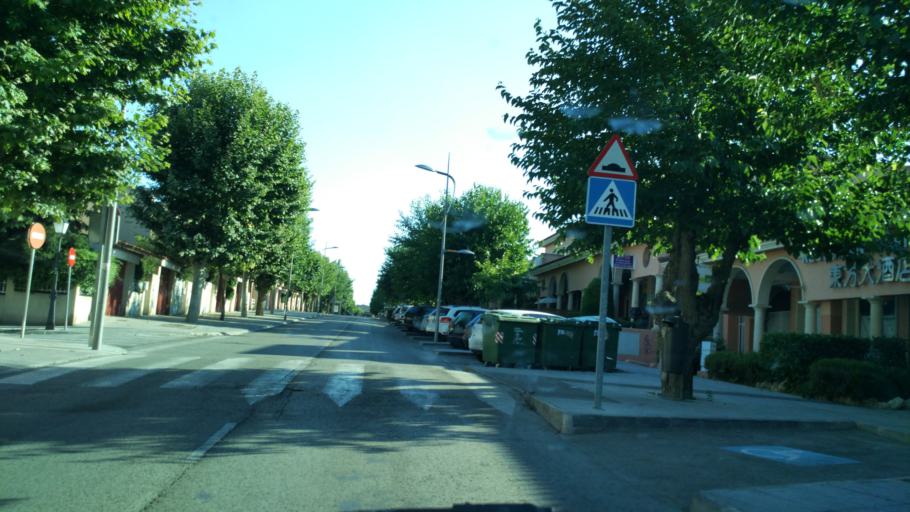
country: ES
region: Madrid
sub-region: Provincia de Madrid
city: San Agustin de Guadalix
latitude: 40.6835
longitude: -3.6120
